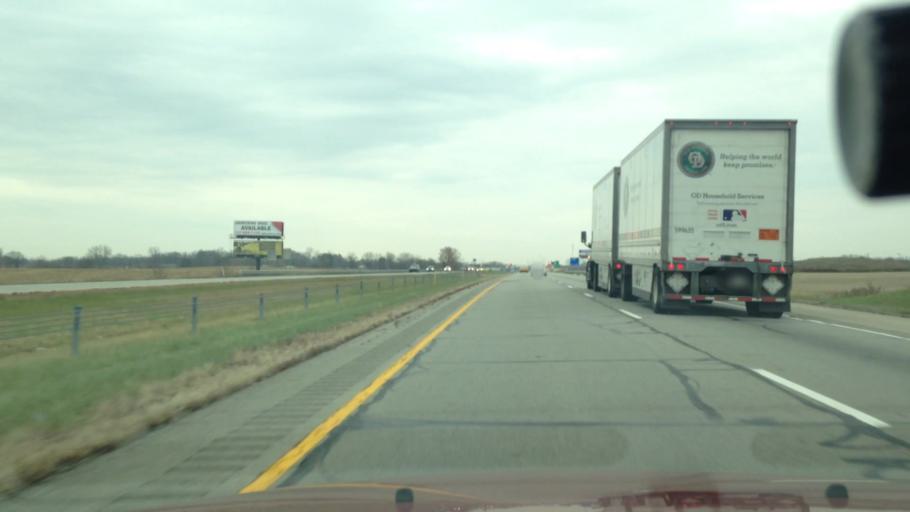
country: US
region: Indiana
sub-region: Wayne County
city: Cambridge City
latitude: 39.8532
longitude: -85.1581
